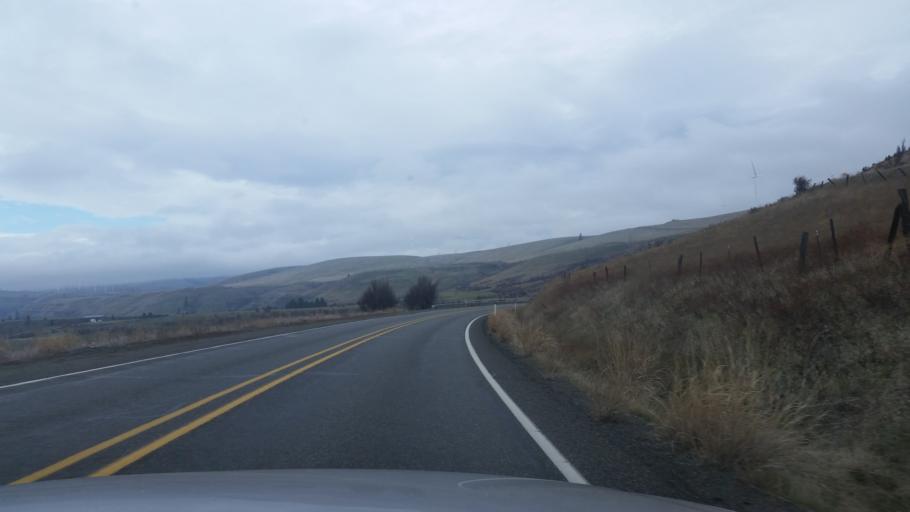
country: US
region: Washington
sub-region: Kittitas County
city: Ellensburg
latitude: 47.1102
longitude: -120.7156
